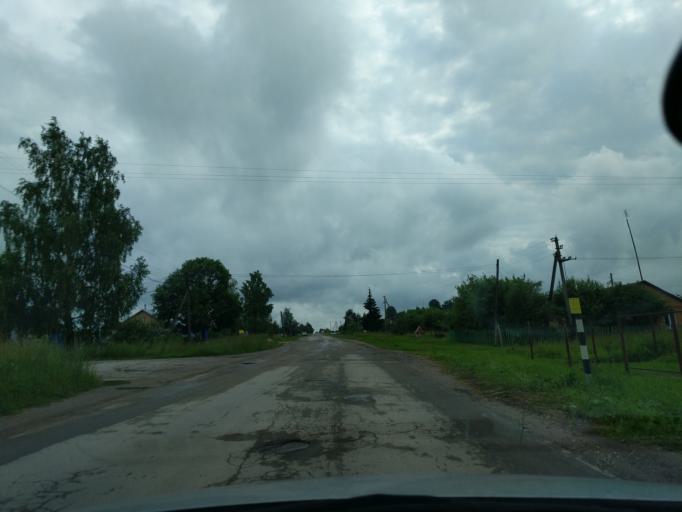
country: RU
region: Kaluga
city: Myatlevo
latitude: 54.7964
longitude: 35.7393
